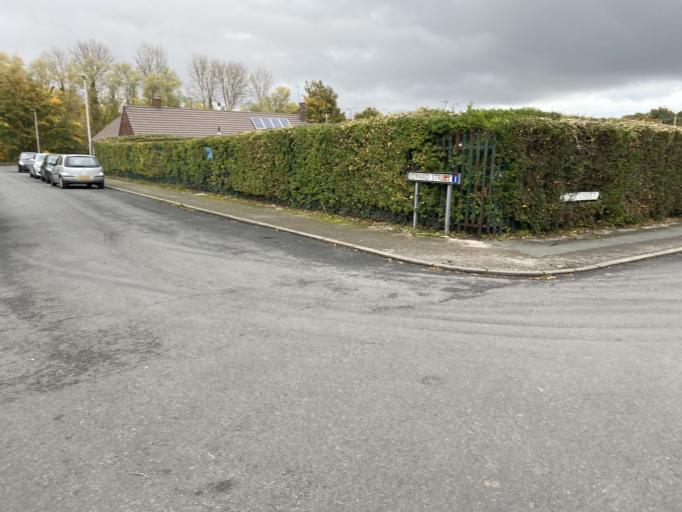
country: GB
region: England
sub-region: Cheshire West and Chester
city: Ellesmere Port
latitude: 53.2872
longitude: -2.8982
